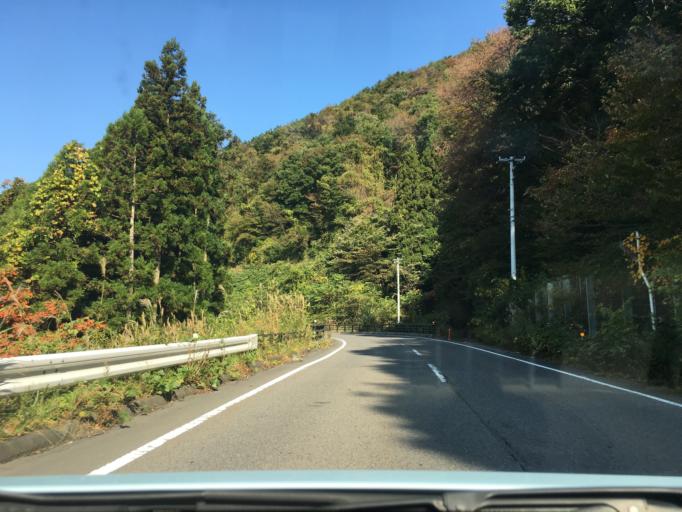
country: JP
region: Fukushima
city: Sukagawa
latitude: 37.2994
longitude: 140.1577
